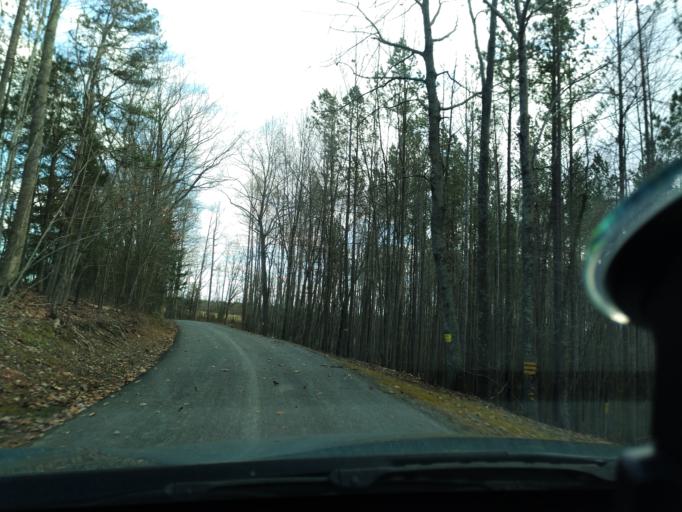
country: US
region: Virginia
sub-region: Nottoway County
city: Crewe
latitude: 37.1763
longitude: -78.2658
